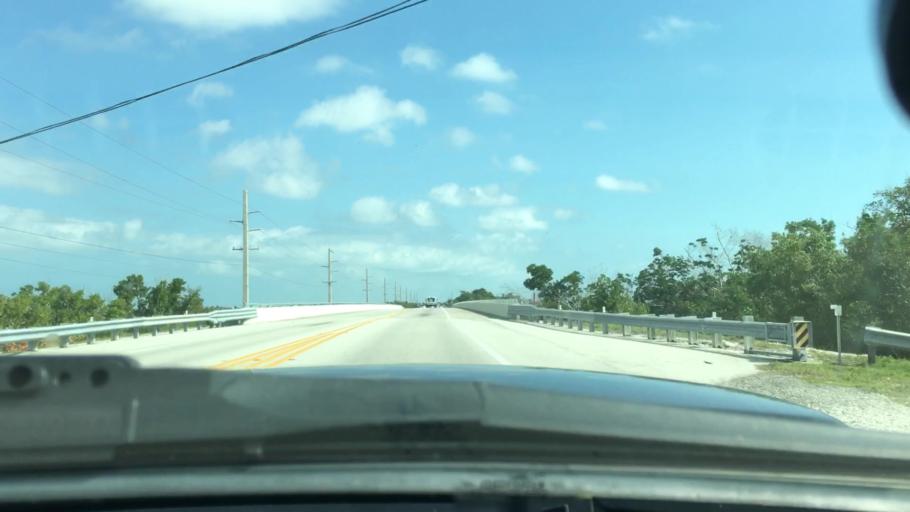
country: US
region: Florida
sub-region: Monroe County
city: Big Pine Key
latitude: 24.6627
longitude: -81.4040
